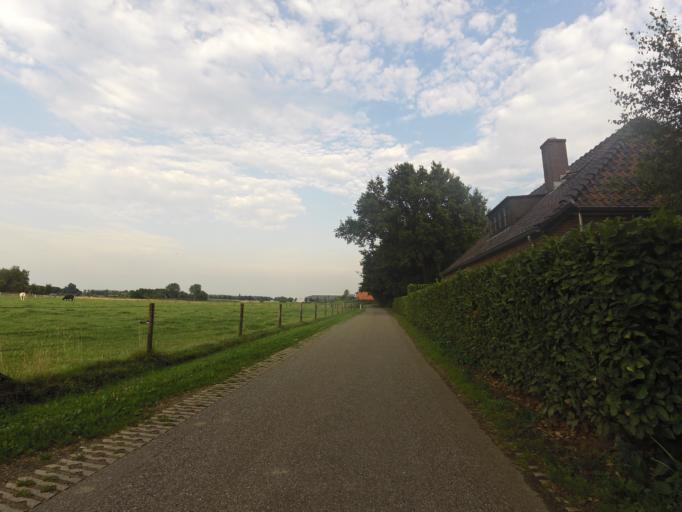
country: NL
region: Gelderland
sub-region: Gemeente Doetinchem
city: Doetinchem
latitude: 51.9244
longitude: 6.3030
